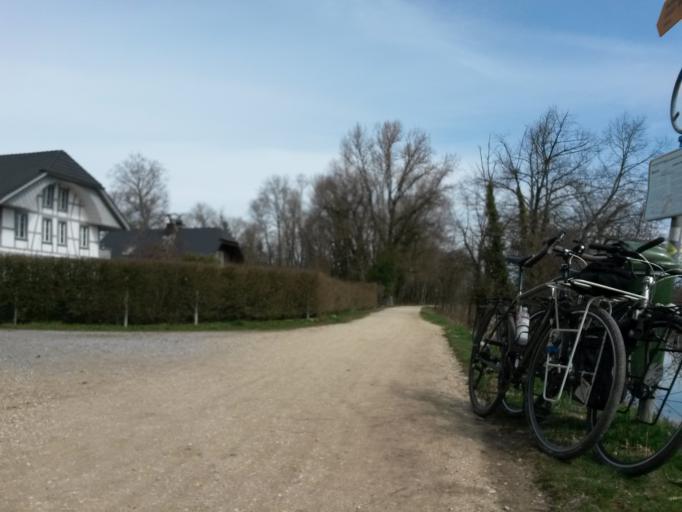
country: CH
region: Bern
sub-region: Biel/Bienne District
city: Orpund
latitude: 47.1340
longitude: 7.3065
